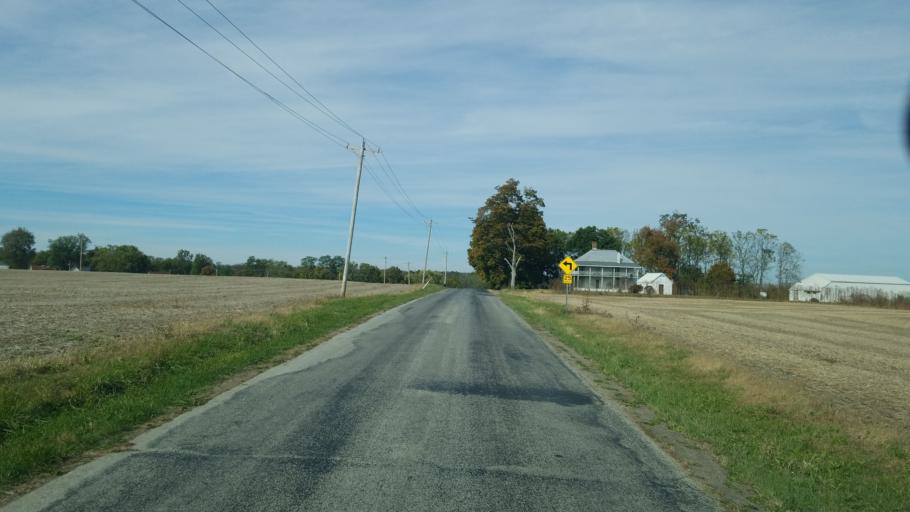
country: US
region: Ohio
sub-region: Highland County
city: Leesburg
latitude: 39.3234
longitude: -83.4733
